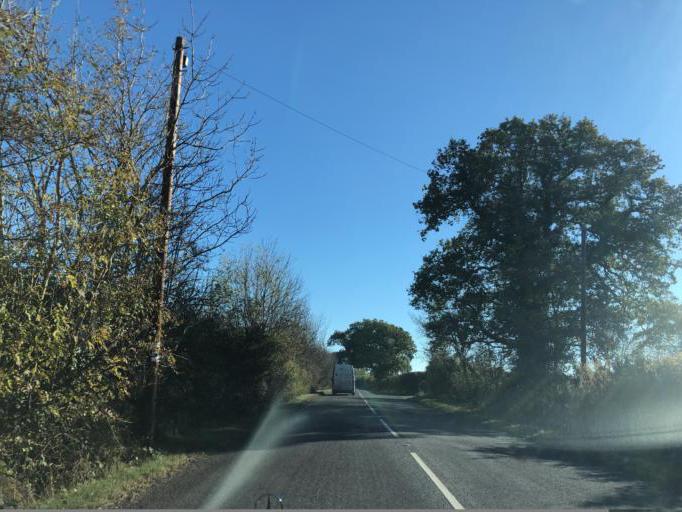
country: GB
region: England
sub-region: Warwickshire
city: Royal Leamington Spa
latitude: 52.2521
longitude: -1.5195
